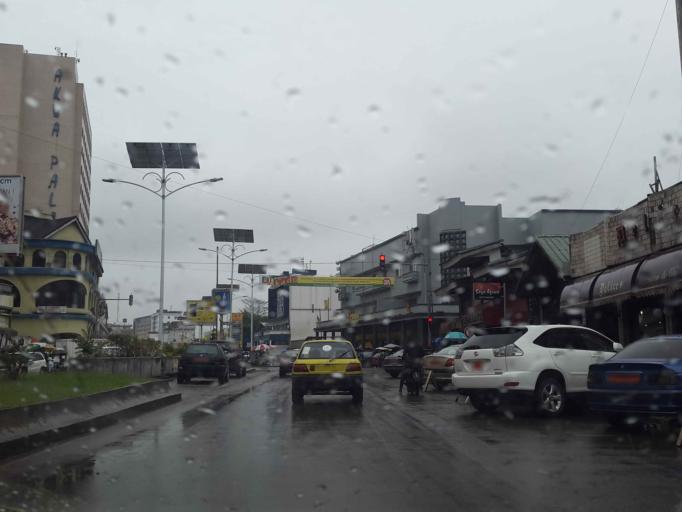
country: CM
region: Littoral
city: Douala
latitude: 4.0513
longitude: 9.6959
